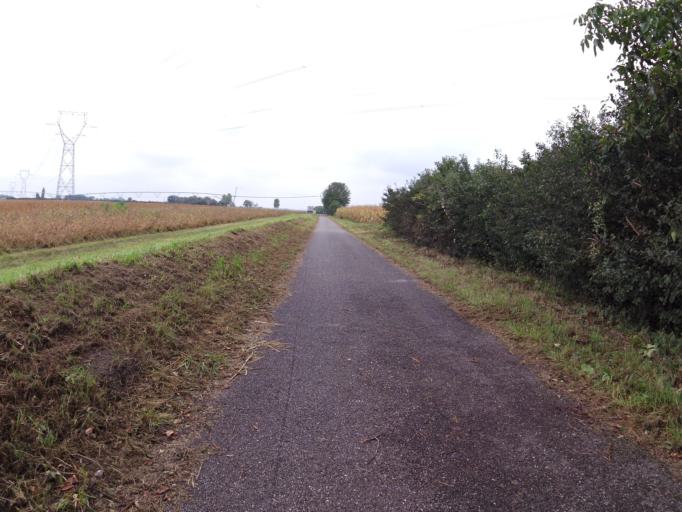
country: FR
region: Alsace
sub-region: Departement du Haut-Rhin
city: Fessenheim
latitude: 47.9404
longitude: 7.5407
